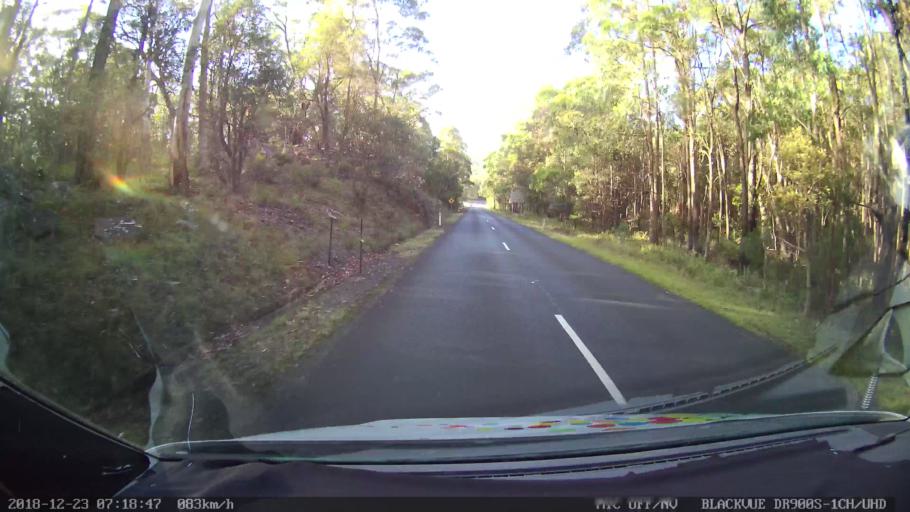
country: AU
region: New South Wales
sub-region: Bellingen
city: Dorrigo
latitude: -30.4787
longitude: 152.2915
